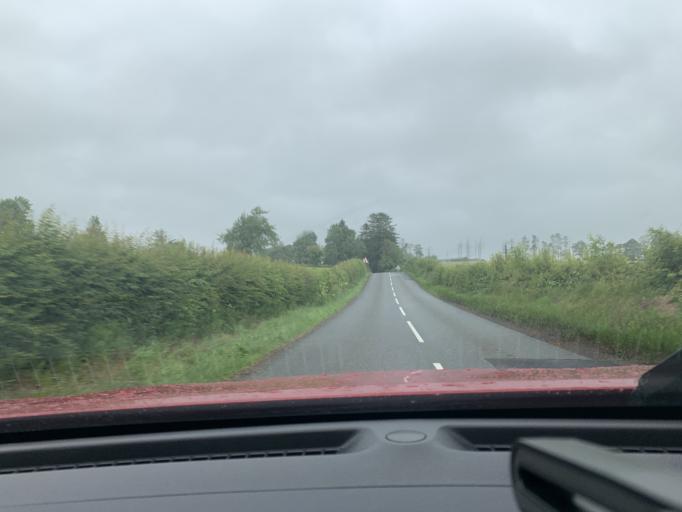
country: GB
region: Northern Ireland
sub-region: Fermanagh District
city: Enniskillen
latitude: 54.3105
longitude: -7.6837
